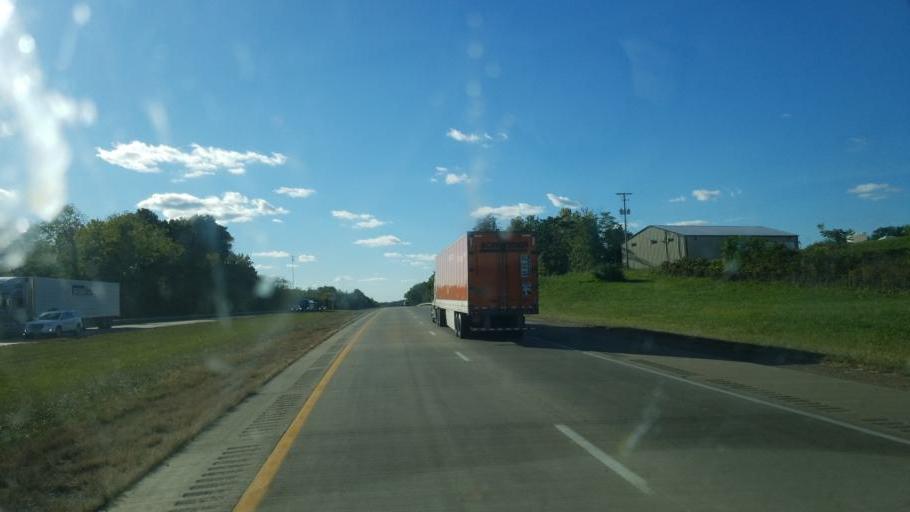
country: US
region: Ohio
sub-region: Belmont County
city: Bethesda
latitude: 40.0566
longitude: -81.0714
